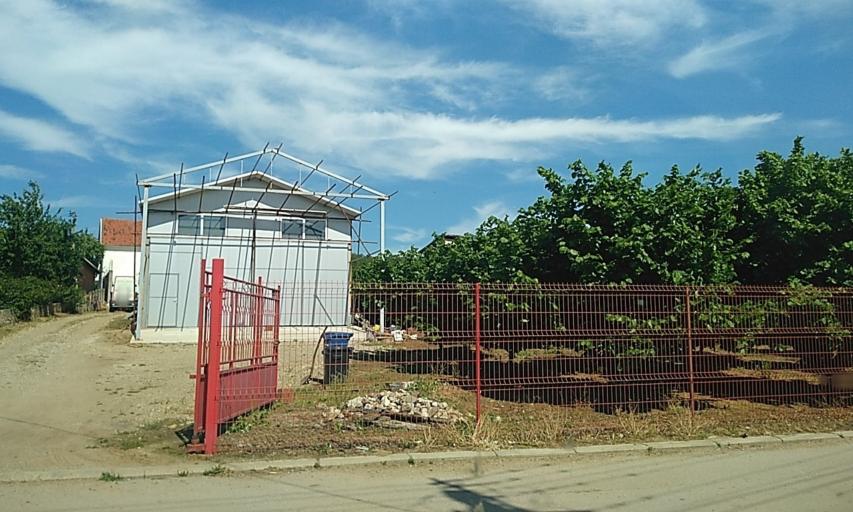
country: RS
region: Central Serbia
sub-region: Nisavski Okrug
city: Nis
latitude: 43.2911
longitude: 21.8649
